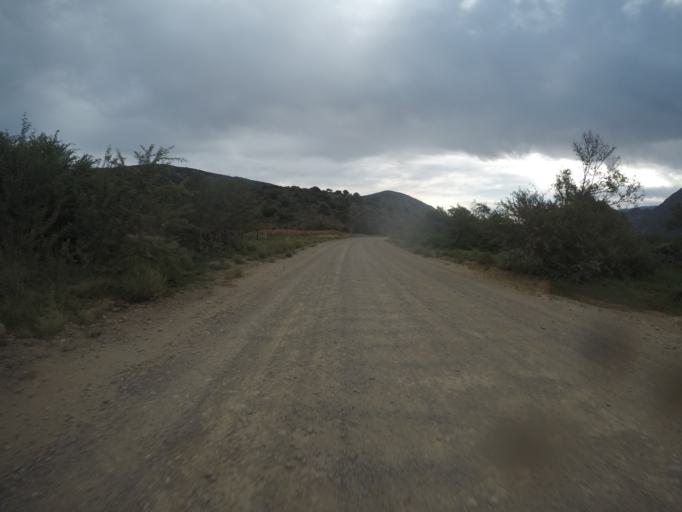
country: ZA
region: Eastern Cape
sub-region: Cacadu District Municipality
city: Willowmore
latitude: -33.5275
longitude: 23.8614
